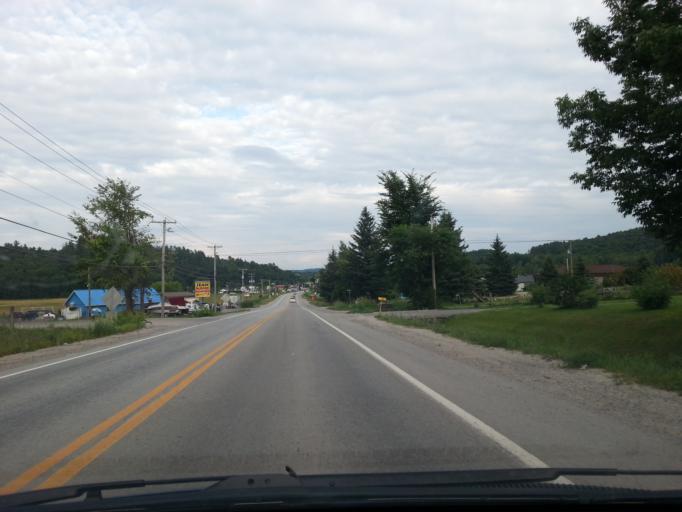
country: CA
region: Quebec
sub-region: Outaouais
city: Wakefield
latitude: 45.6210
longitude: -75.9278
